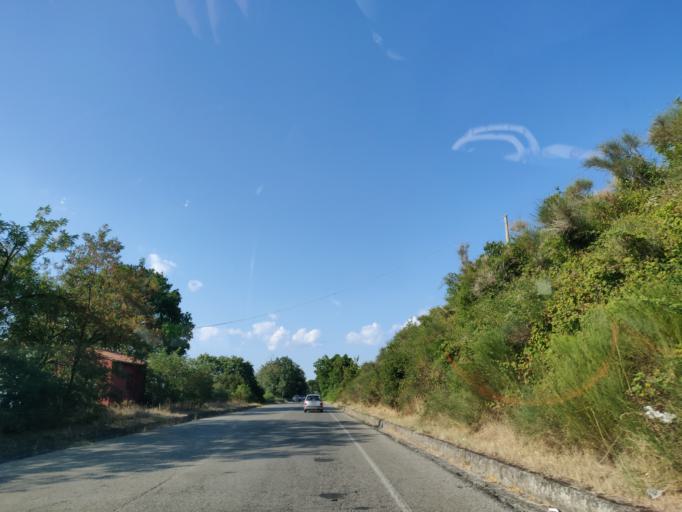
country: IT
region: Latium
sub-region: Provincia di Viterbo
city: Valentano
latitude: 42.5865
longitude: 11.8351
